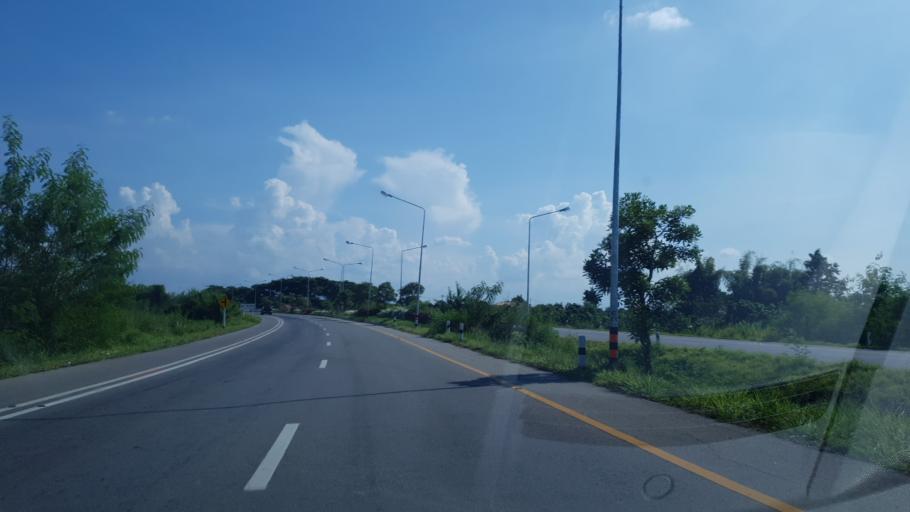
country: TH
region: Lamphun
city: Pa Sang
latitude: 18.5481
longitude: 98.8493
